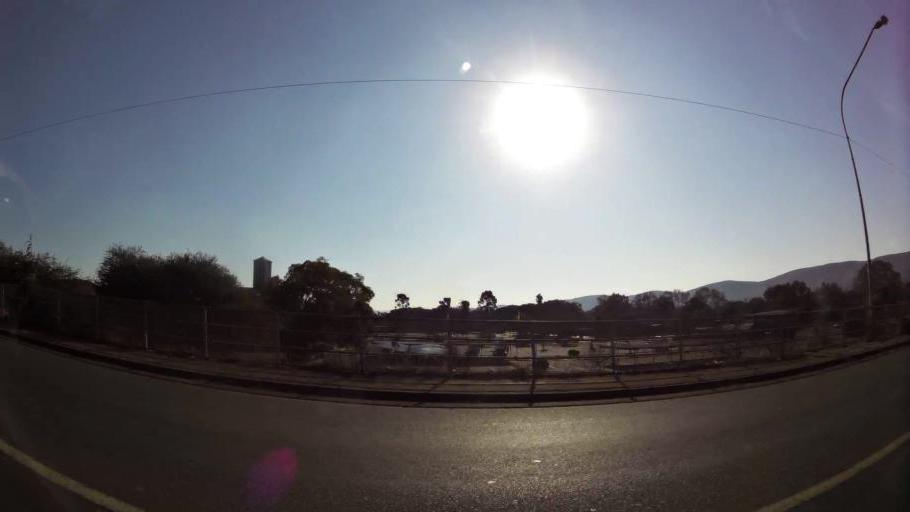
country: ZA
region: Gauteng
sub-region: City of Tshwane Metropolitan Municipality
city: Pretoria
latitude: -25.7174
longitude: 28.1543
